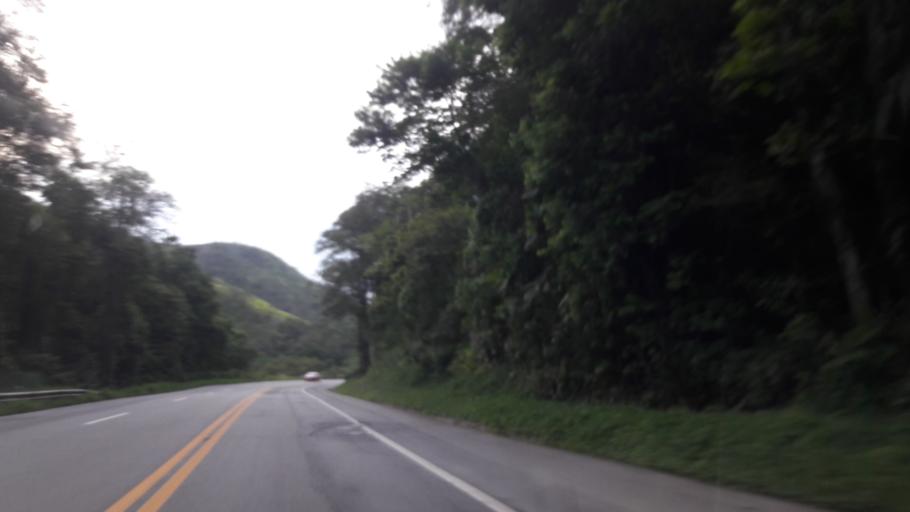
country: BR
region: Sao Paulo
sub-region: Miracatu
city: Miracatu
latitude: -24.2688
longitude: -47.2886
